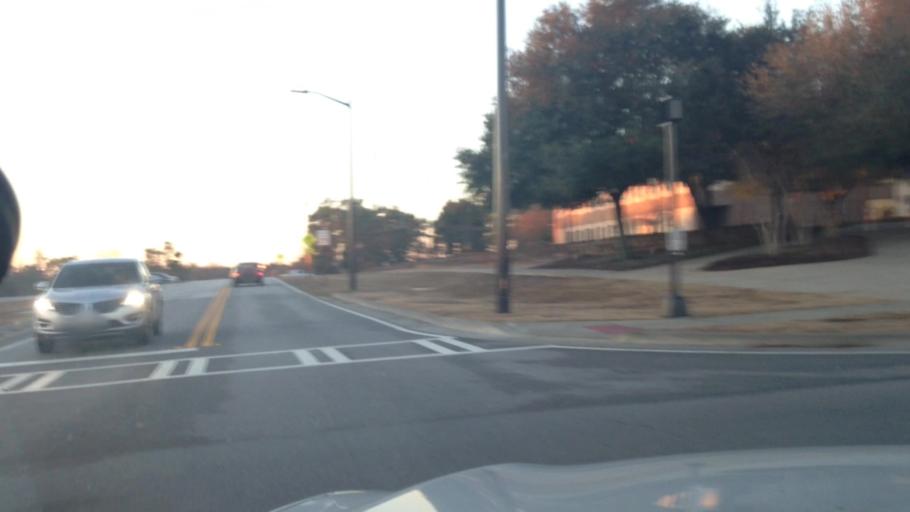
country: US
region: Georgia
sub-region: Columbia County
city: Grovetown
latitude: 33.4251
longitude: -82.1354
